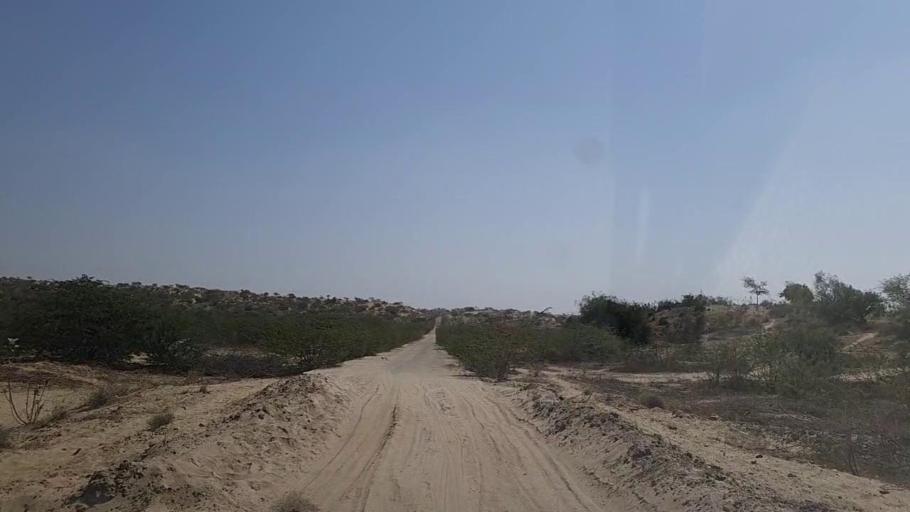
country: PK
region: Sindh
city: Diplo
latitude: 24.4934
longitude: 69.4346
